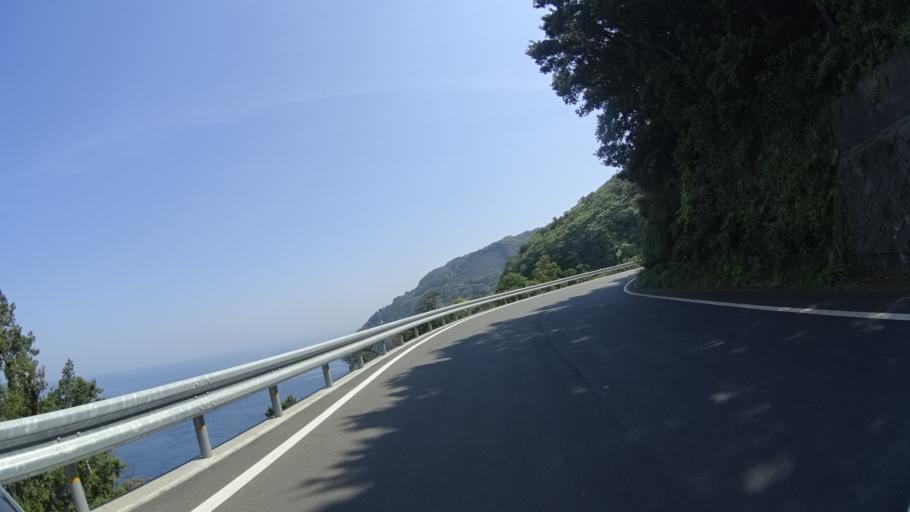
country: JP
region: Oita
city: Tsukumiura
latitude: 33.3570
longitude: 132.0320
